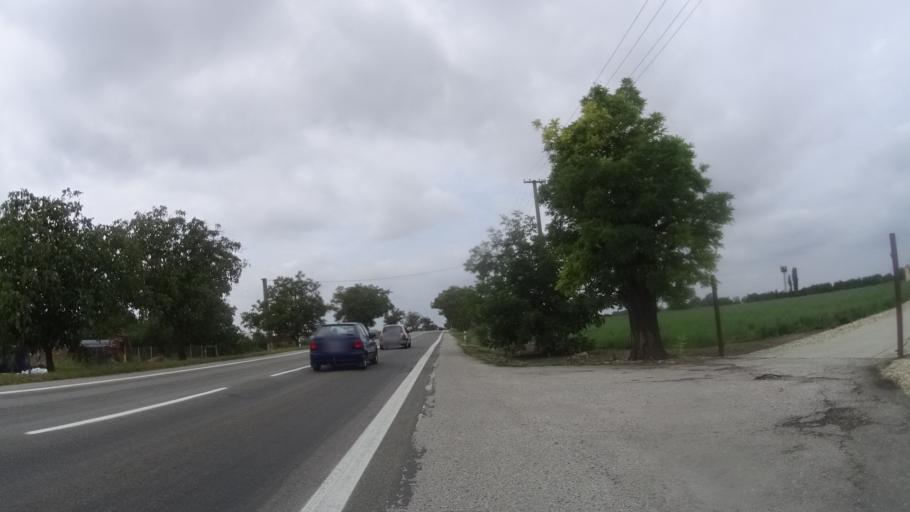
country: HU
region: Komarom-Esztergom
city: Acs
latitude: 47.7663
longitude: 18.0285
